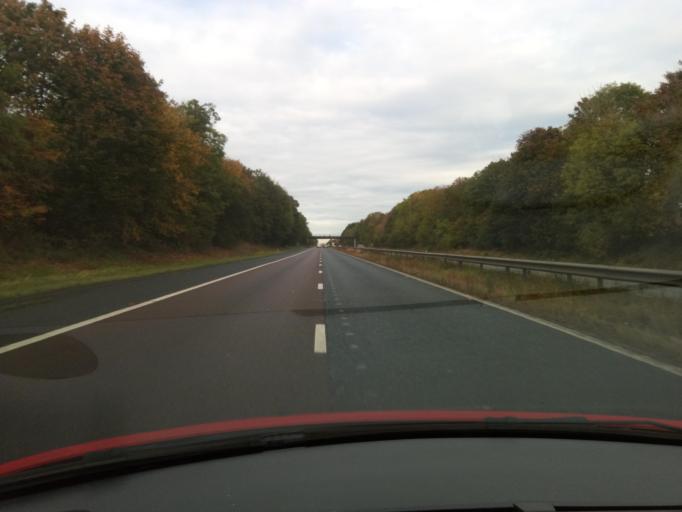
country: GB
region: England
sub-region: Darlington
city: High Coniscliffe
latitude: 54.5209
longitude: -1.6211
